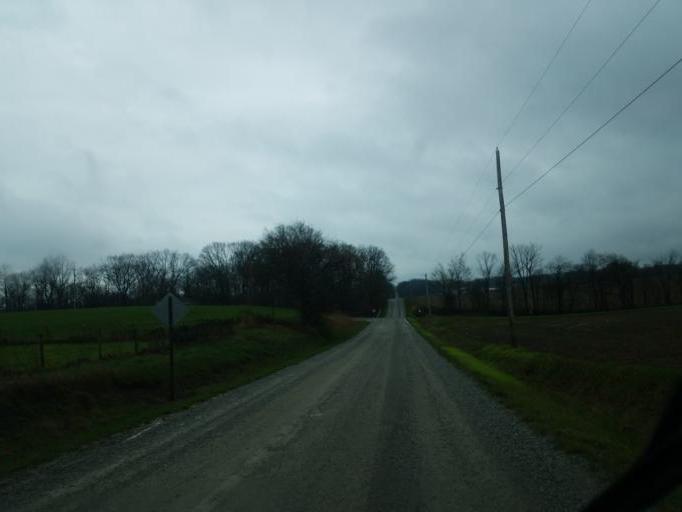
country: US
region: Ohio
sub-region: Morrow County
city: Mount Gilead
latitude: 40.4782
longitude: -82.7227
